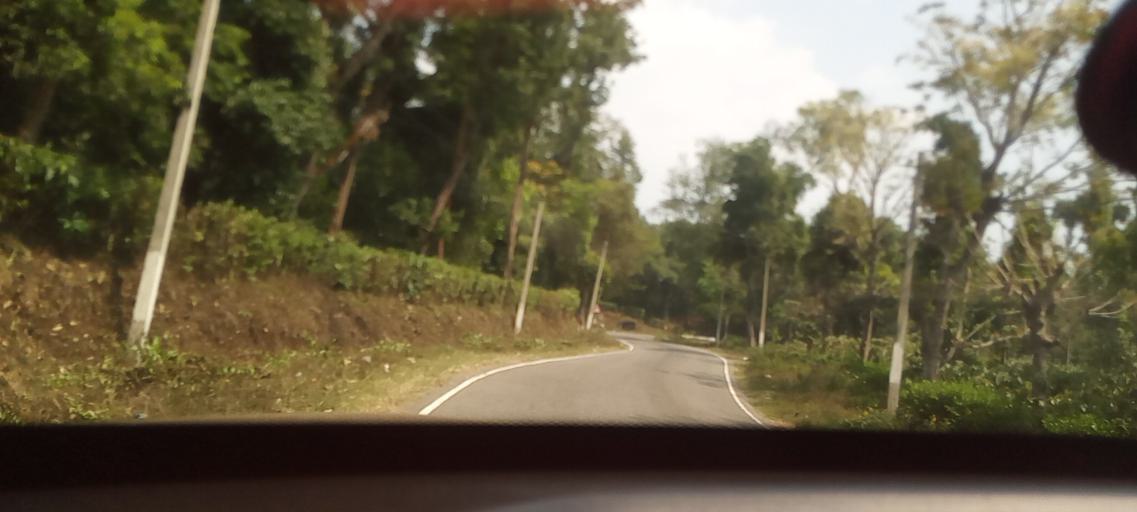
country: IN
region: Karnataka
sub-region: Chikmagalur
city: Mudigere
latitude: 13.2554
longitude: 75.6374
